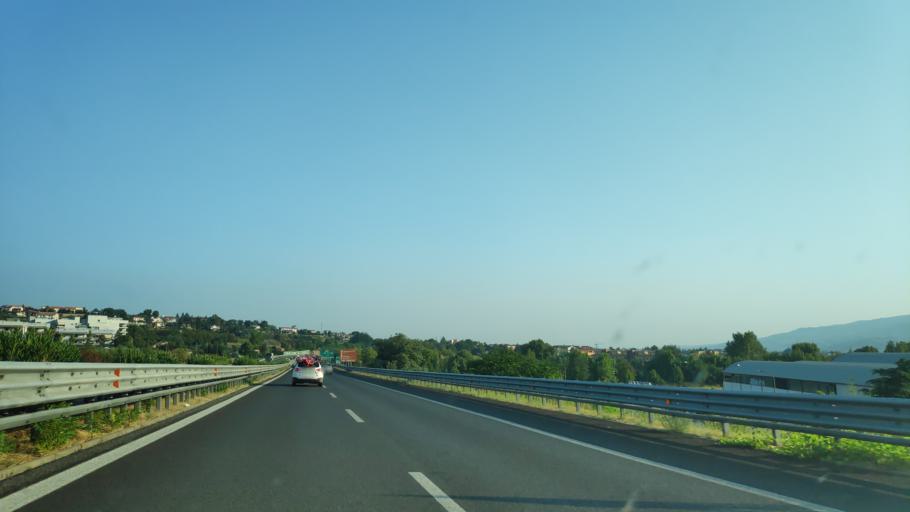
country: IT
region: Calabria
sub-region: Provincia di Cosenza
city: Quattromiglia
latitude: 39.3355
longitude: 16.2365
